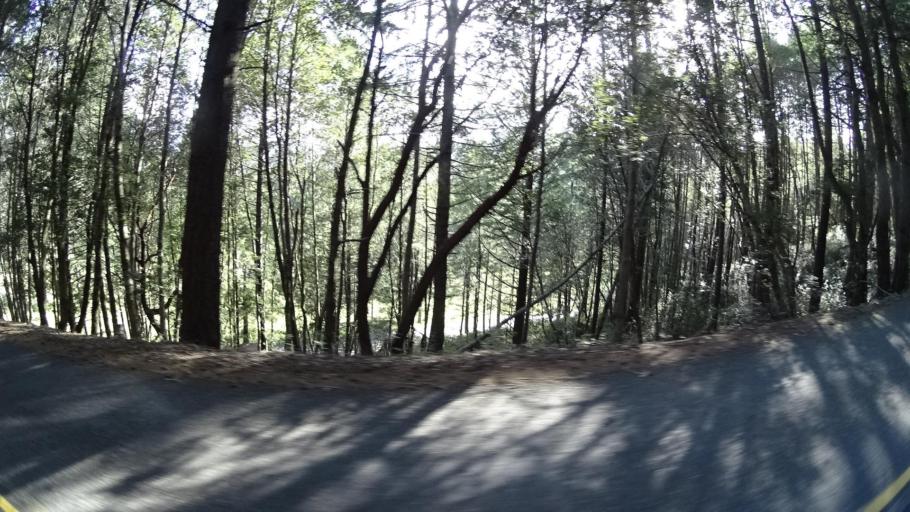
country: US
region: California
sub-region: Humboldt County
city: Rio Dell
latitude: 40.3316
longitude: -124.0352
